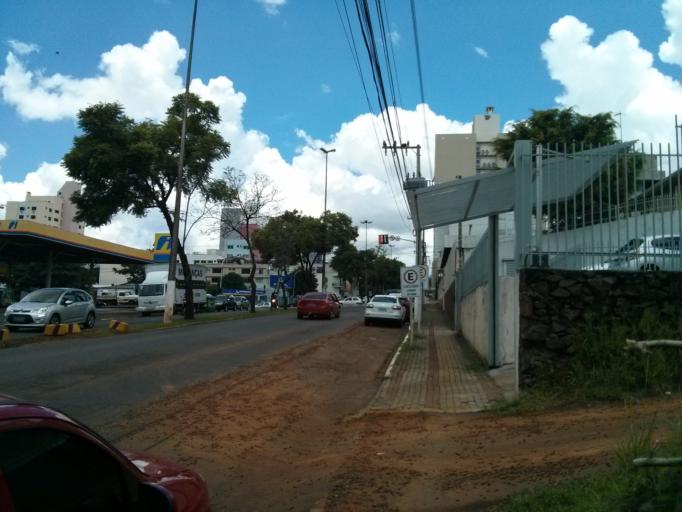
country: BR
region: Santa Catarina
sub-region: Chapeco
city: Chapeco
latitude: -27.1020
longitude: -52.6202
